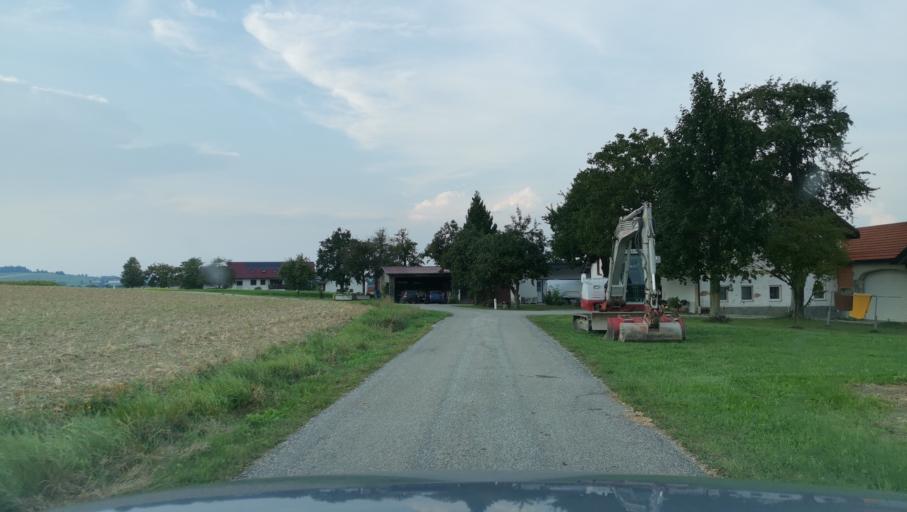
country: AT
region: Upper Austria
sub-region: Politischer Bezirk Grieskirchen
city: Grieskirchen
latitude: 48.3062
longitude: 13.8089
